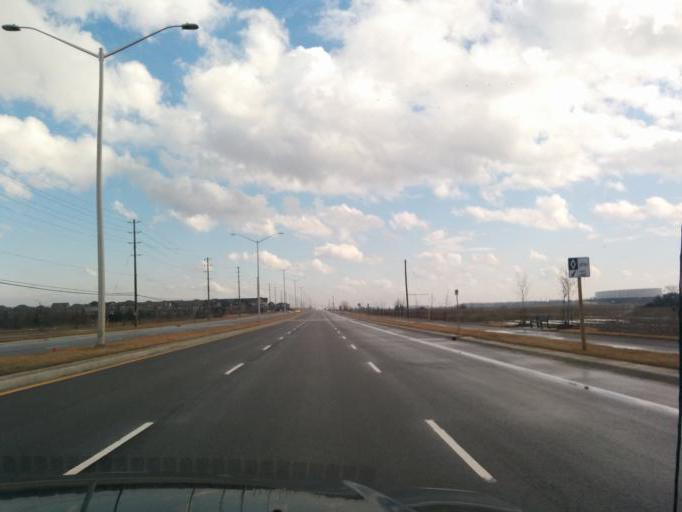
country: CA
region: Ontario
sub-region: Halton
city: Milton
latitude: 43.4838
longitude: -79.8811
